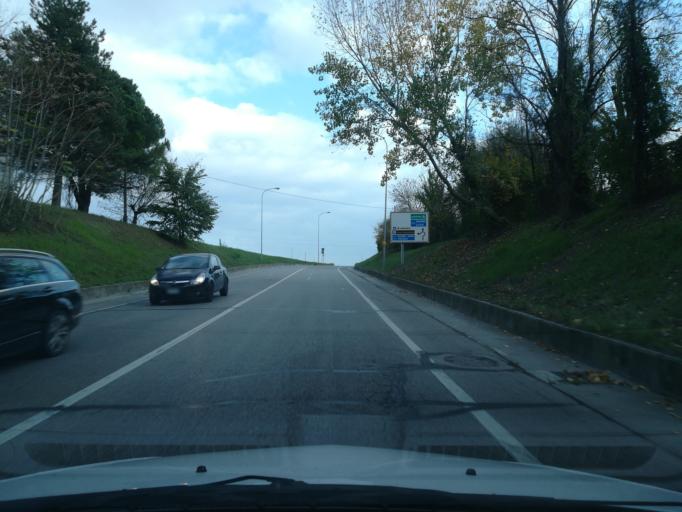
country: IT
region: Emilia-Romagna
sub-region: Provincia di Bologna
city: Imola
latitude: 44.3533
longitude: 11.7360
